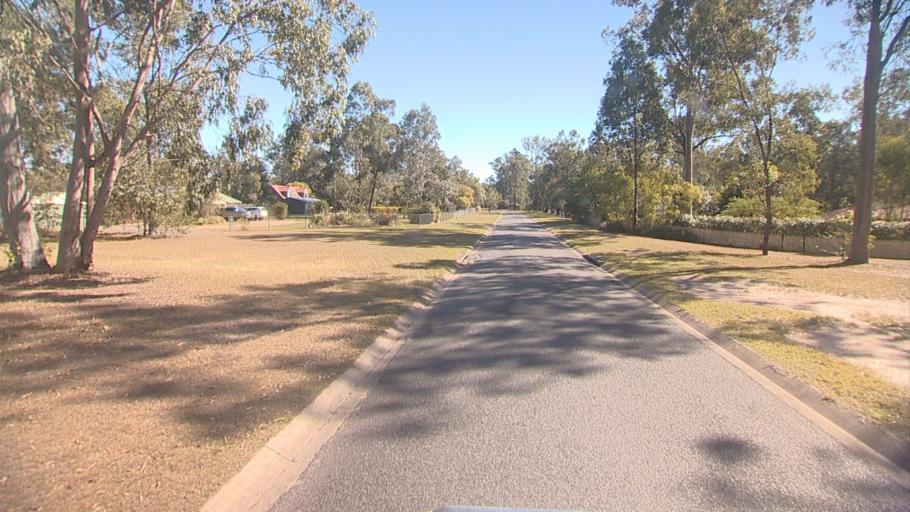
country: AU
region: Queensland
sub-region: Logan
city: North Maclean
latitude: -27.8153
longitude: 152.9530
